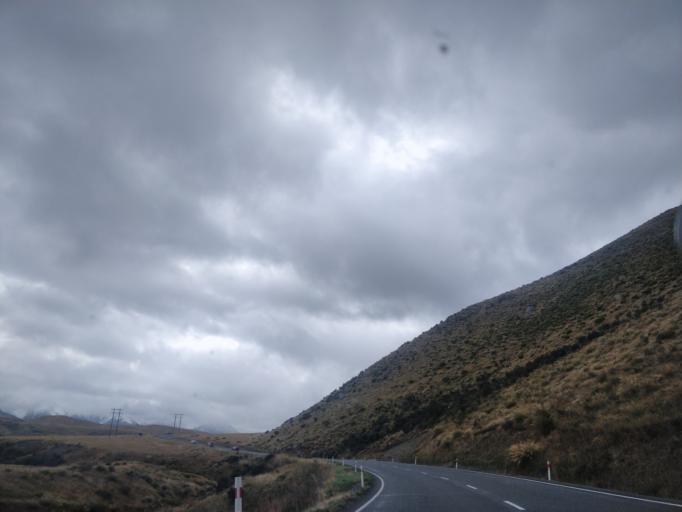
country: NZ
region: Canterbury
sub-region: Ashburton District
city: Methven
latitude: -43.2627
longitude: 171.7110
